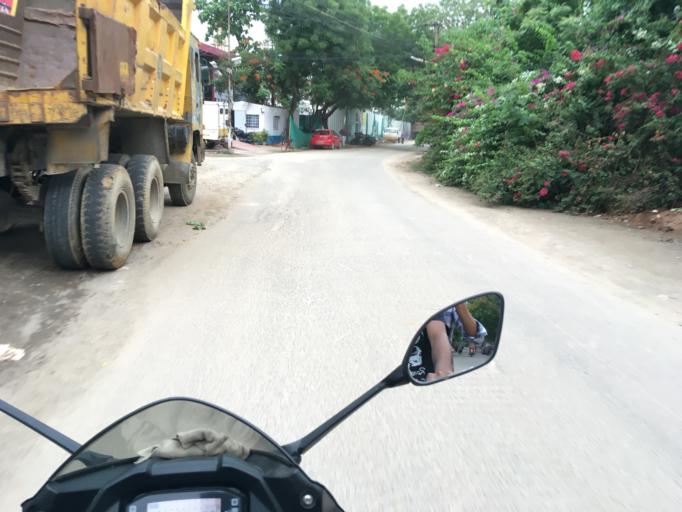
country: IN
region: Telangana
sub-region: Rangareddi
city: Kukatpalli
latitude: 17.4479
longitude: 78.3859
